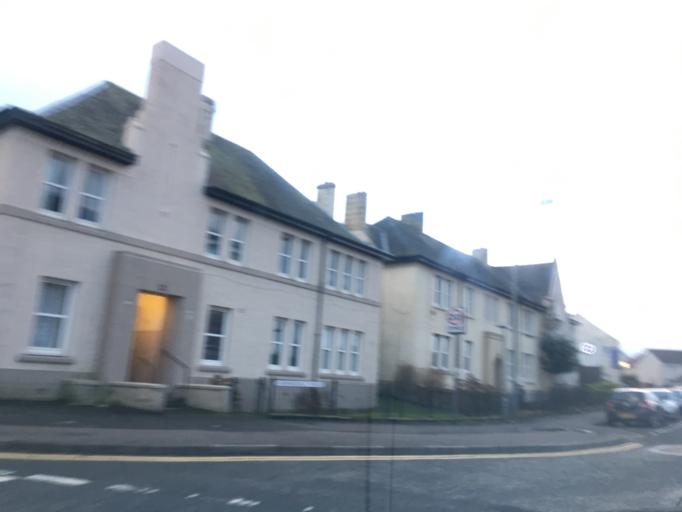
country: GB
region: Scotland
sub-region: Stirling
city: Stirling
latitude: 56.0988
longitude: -3.9375
